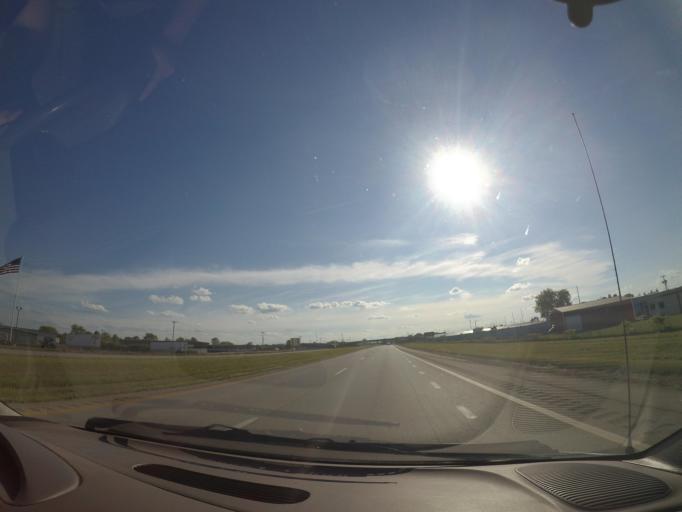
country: US
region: Ohio
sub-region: Henry County
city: Napoleon
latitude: 41.4128
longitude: -84.1140
